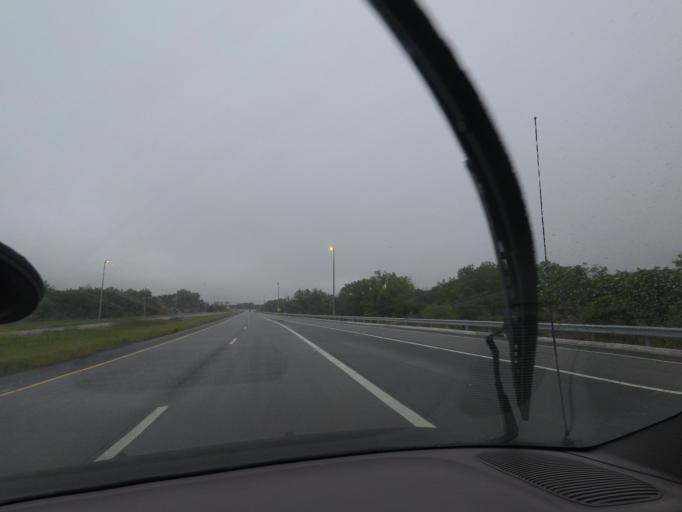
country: US
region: Illinois
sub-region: Macon County
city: Harristown
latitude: 39.8398
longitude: -89.0414
